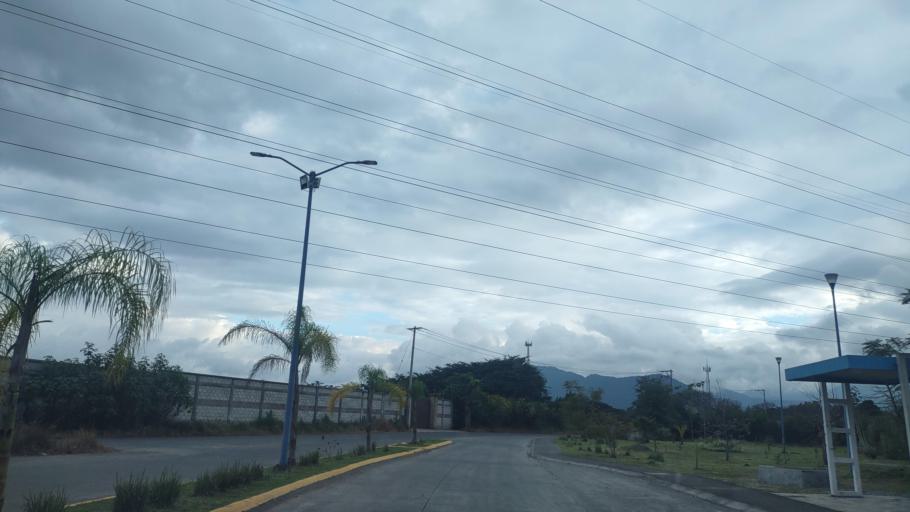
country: MX
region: Veracruz
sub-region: Ixtaczoquitlan
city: Buenavista
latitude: 18.8816
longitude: -97.0583
